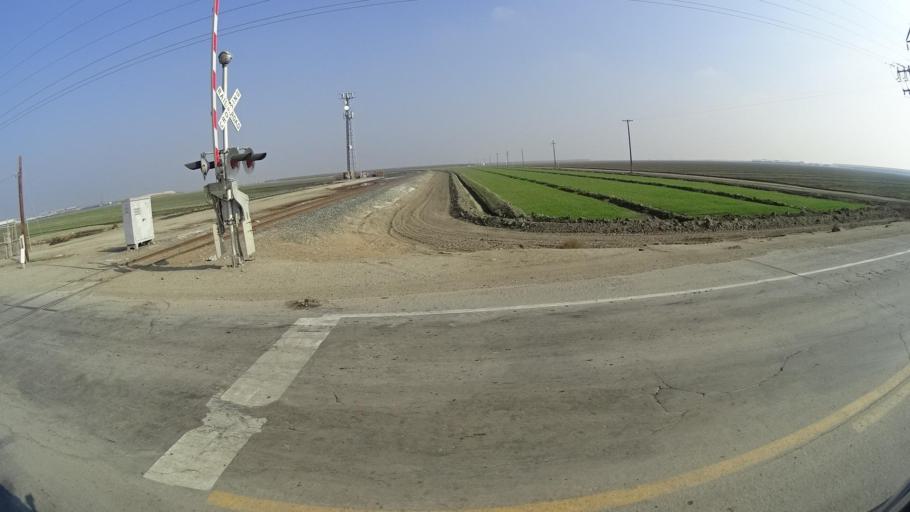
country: US
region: California
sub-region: Kern County
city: Greenfield
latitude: 35.1800
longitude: -119.1103
